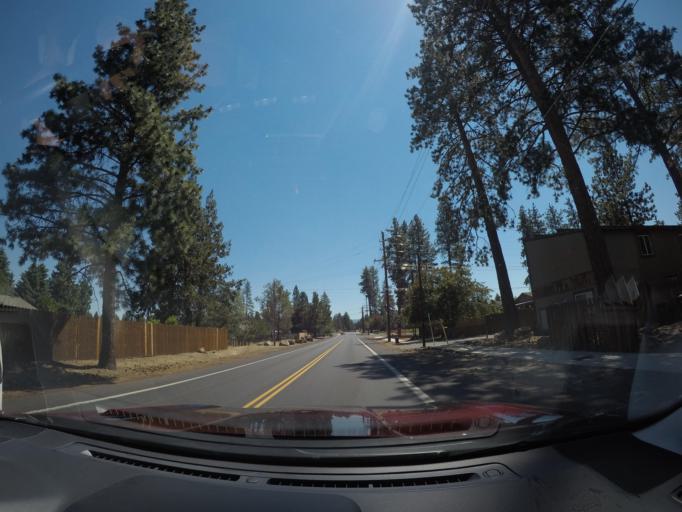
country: US
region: Oregon
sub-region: Deschutes County
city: Sisters
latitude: 44.2930
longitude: -121.5437
